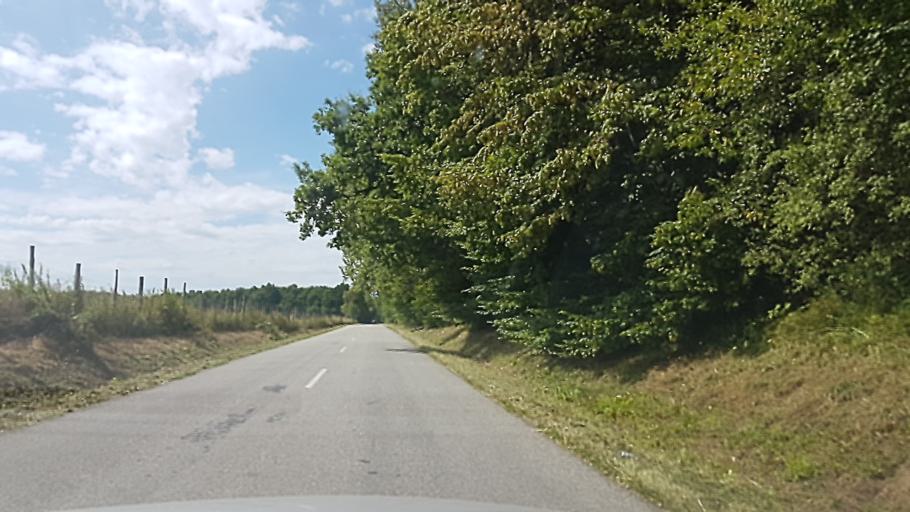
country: HU
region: Somogy
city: Barcs
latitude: 45.9384
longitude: 17.6408
